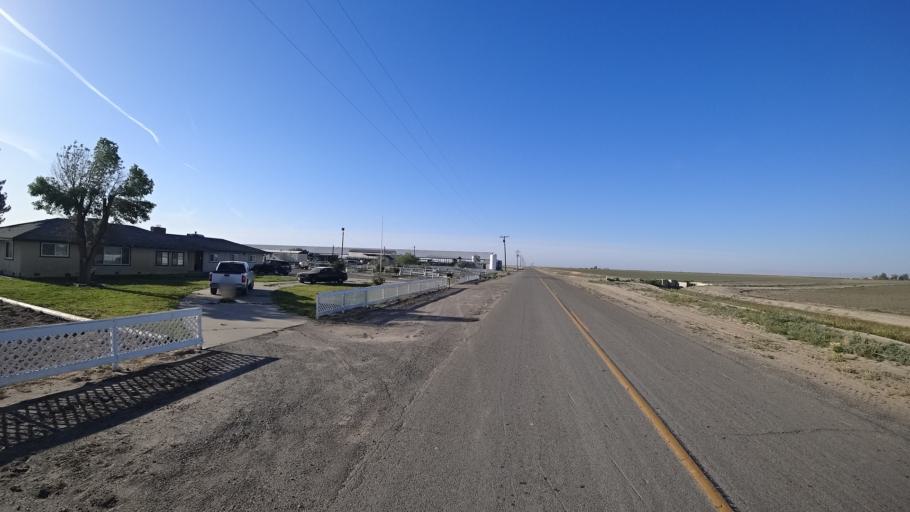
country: US
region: California
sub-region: Kings County
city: Stratford
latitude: 36.1673
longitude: -119.7981
